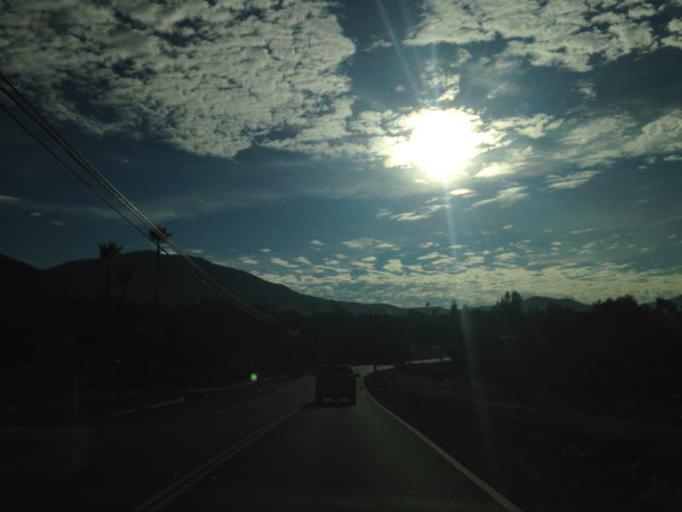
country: US
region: California
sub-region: San Diego County
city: Valley Center
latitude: 33.3395
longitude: -117.0093
